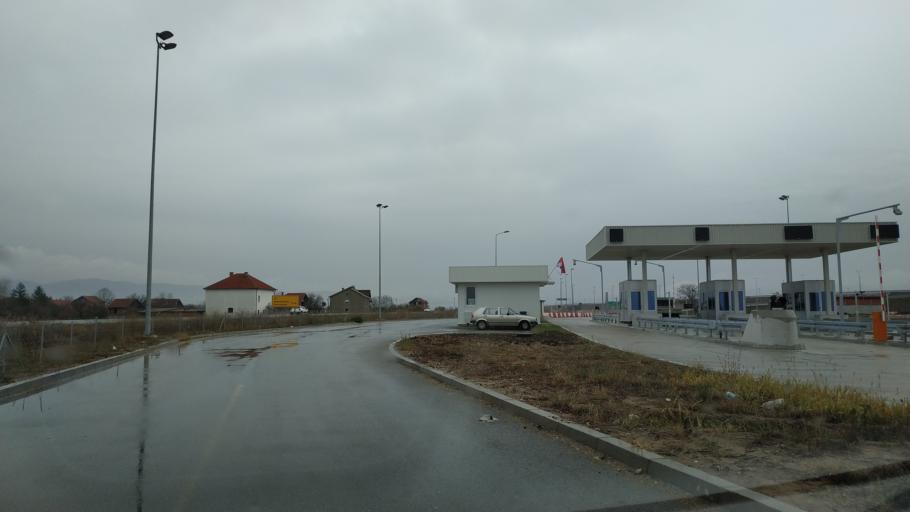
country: RS
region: Central Serbia
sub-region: Pirotski Okrug
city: Pirot
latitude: 43.1240
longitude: 22.6184
